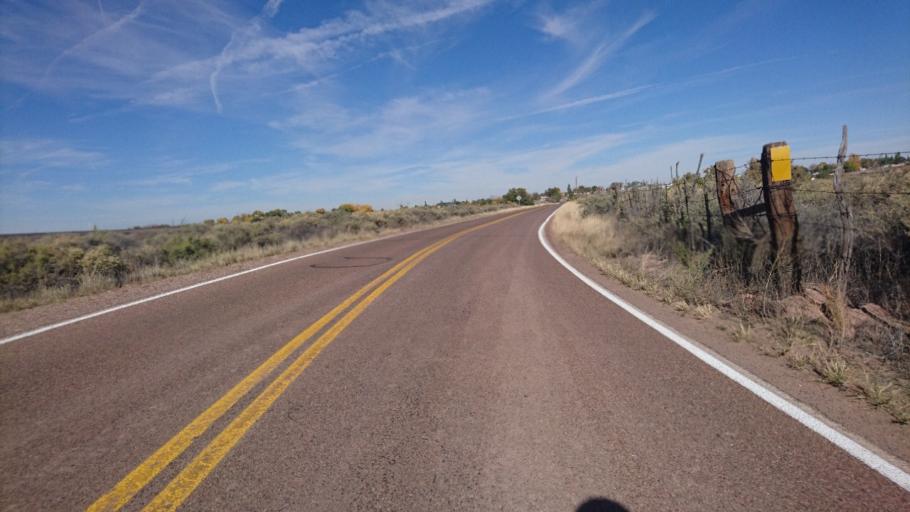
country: US
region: Arizona
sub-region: Navajo County
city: Joseph City
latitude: 34.9476
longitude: -110.3307
